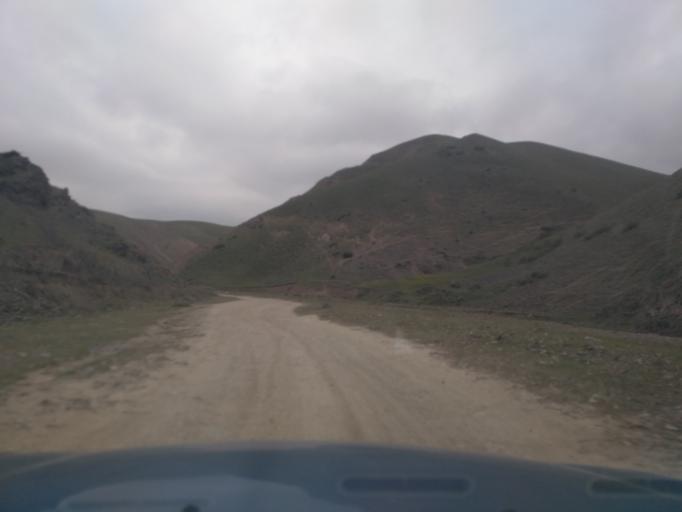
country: UZ
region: Jizzax
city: Zomin
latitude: 39.8476
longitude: 68.3978
